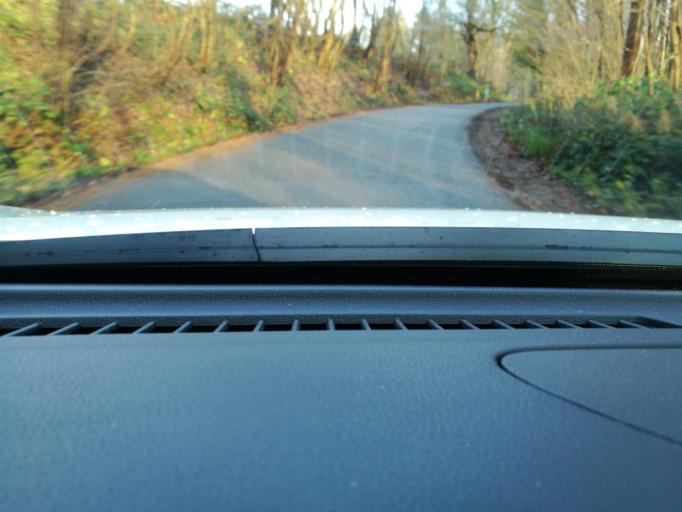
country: DE
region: Schleswig-Holstein
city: Ascheffel
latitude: 54.4248
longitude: 9.7028
